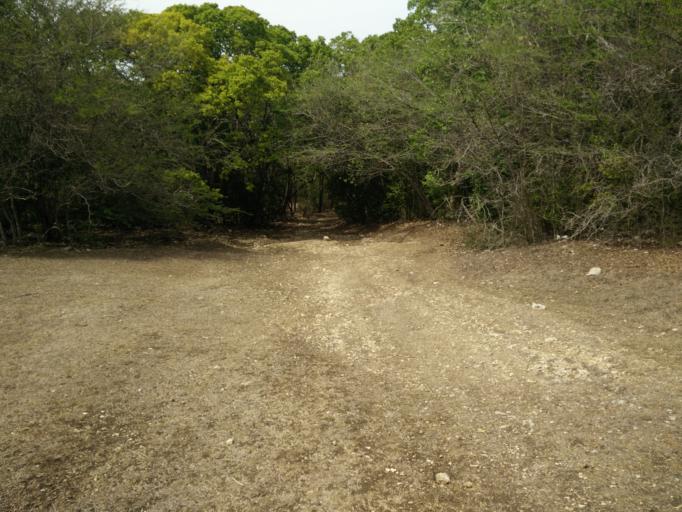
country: GP
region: Guadeloupe
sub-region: Guadeloupe
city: Anse-Bertrand
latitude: 16.4846
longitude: -61.4968
